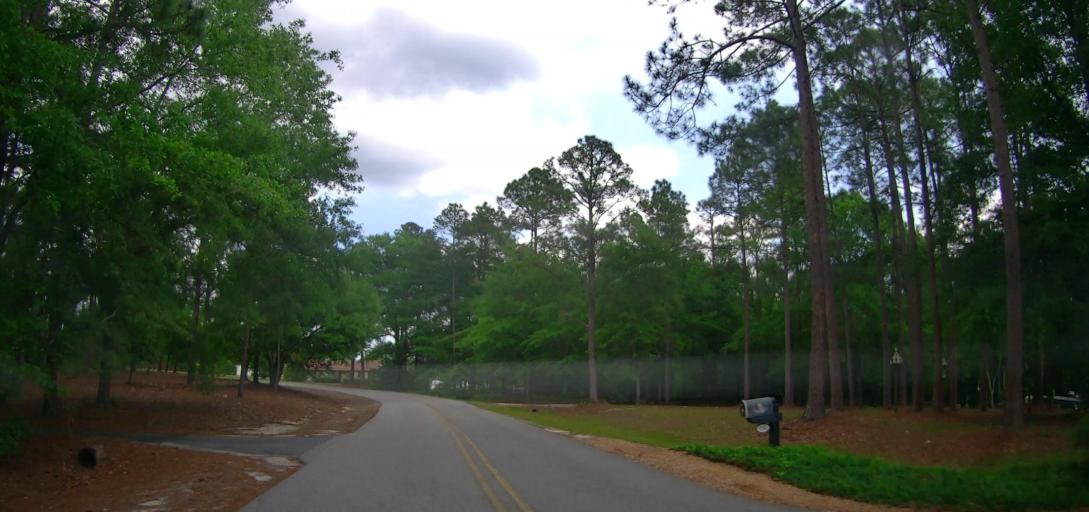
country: US
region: Georgia
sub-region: Treutlen County
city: Soperton
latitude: 32.3640
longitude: -82.5853
